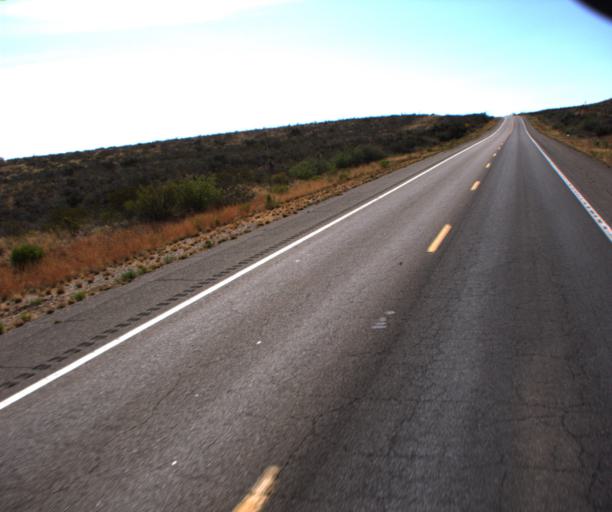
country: US
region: Arizona
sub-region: Cochise County
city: Tombstone
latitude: 31.6950
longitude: -110.0422
